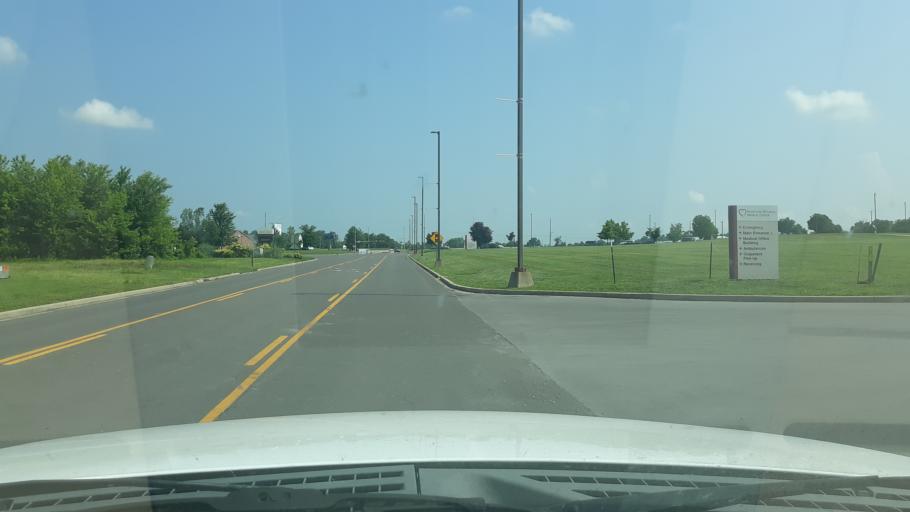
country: US
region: Illinois
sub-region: Williamson County
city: Energy
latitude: 37.7415
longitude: -88.9932
